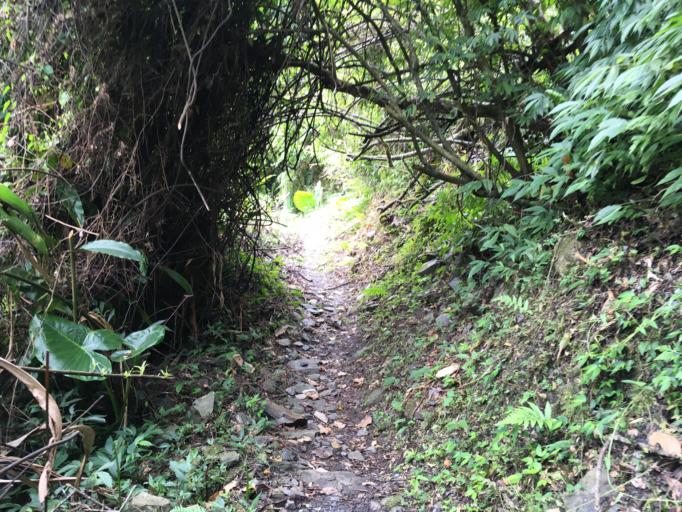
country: TW
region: Taiwan
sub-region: Yilan
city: Yilan
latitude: 24.4230
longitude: 121.6950
